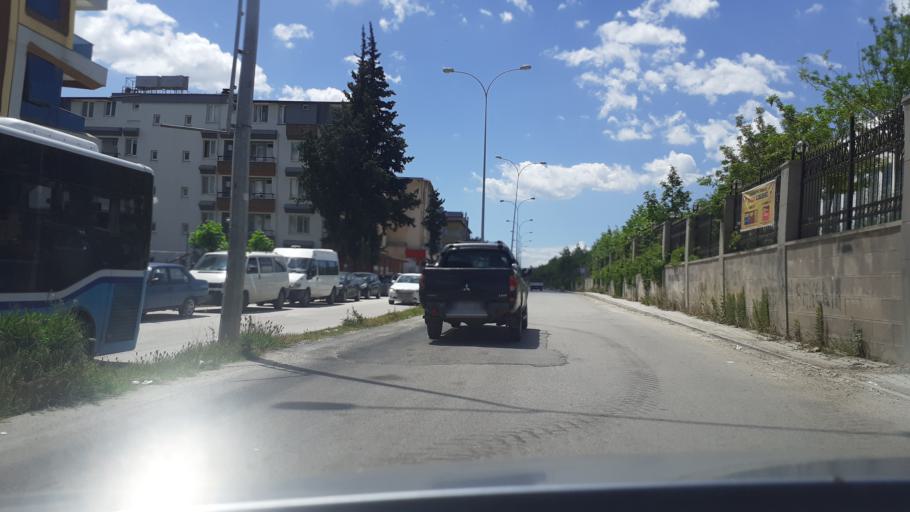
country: TR
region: Hatay
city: Anayazi
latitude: 36.3368
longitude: 36.2001
